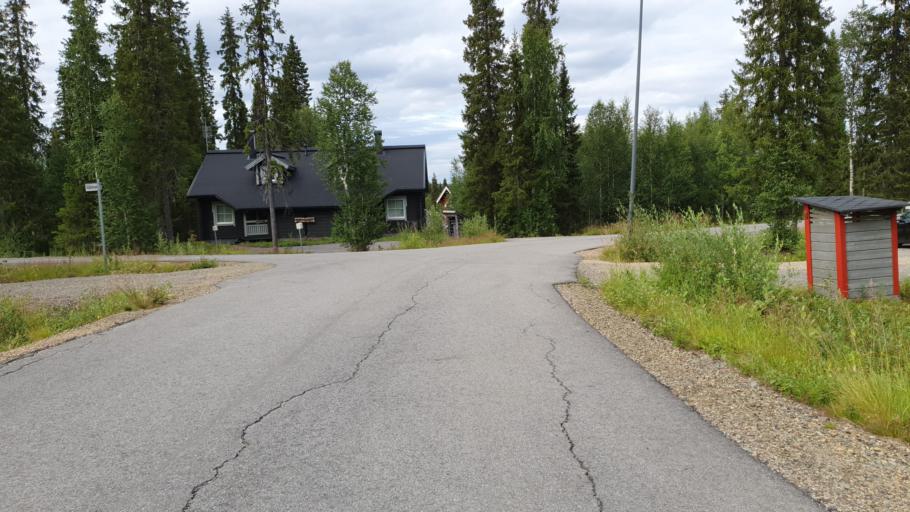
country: FI
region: Lapland
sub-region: Tunturi-Lappi
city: Kolari
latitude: 67.6011
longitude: 24.1426
